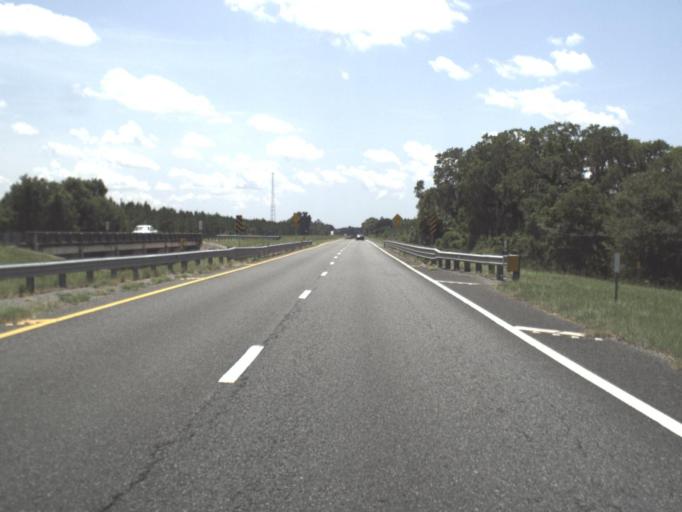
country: US
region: Florida
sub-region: Taylor County
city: Steinhatchee
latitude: 29.7690
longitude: -83.3228
